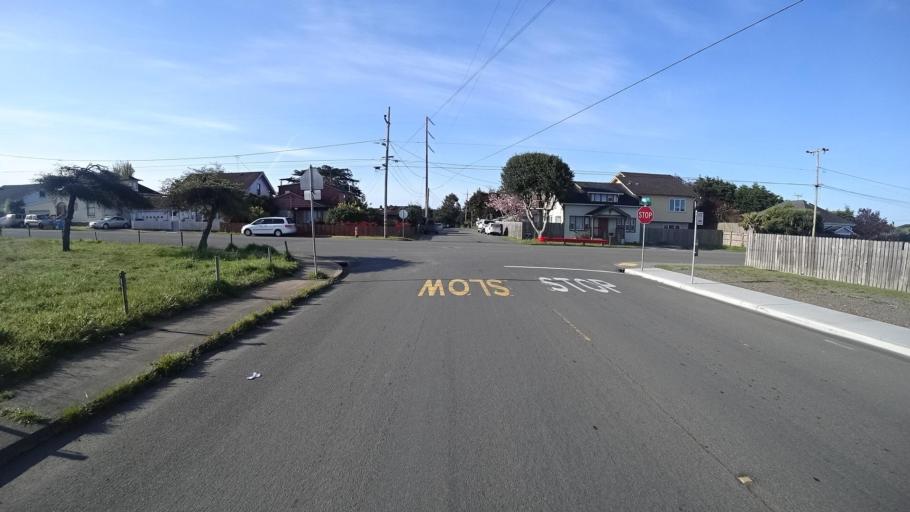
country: US
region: California
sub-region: Humboldt County
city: Bayview
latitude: 40.7735
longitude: -124.1801
